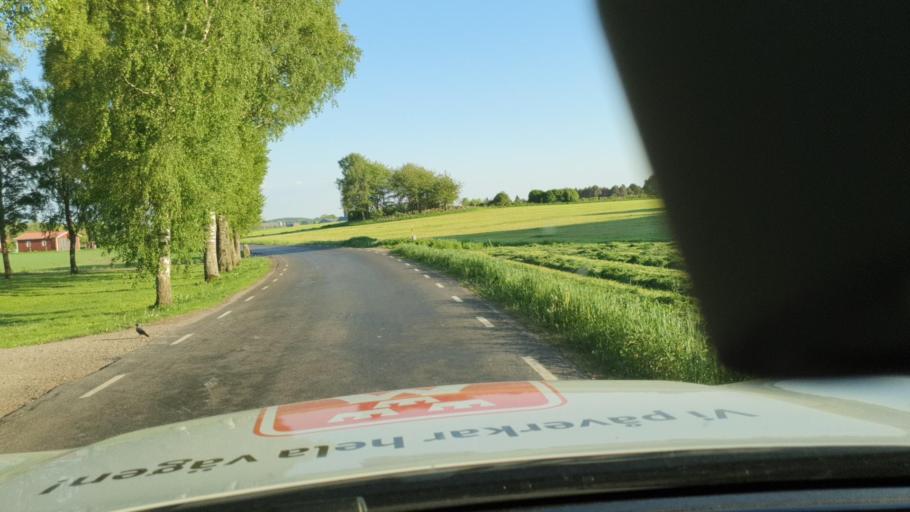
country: SE
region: Vaestra Goetaland
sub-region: Falkopings Kommun
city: Falkoeping
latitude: 58.0841
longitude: 13.6327
